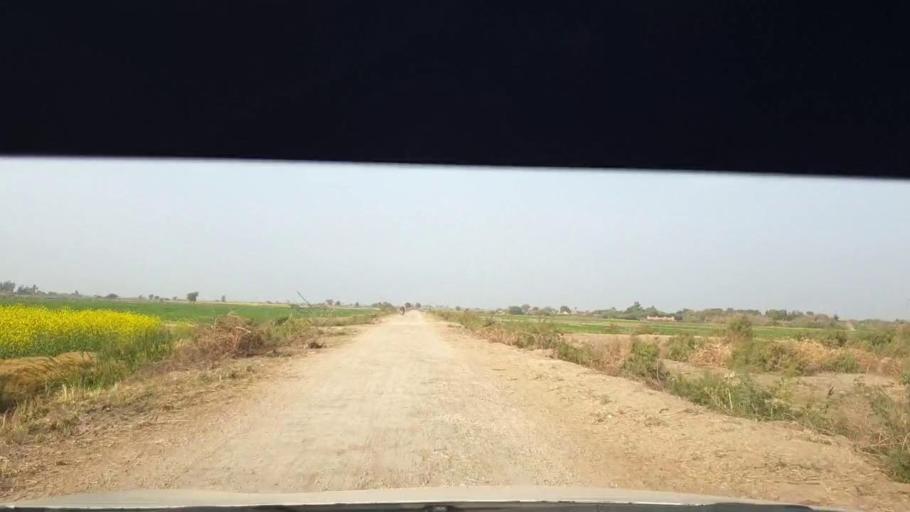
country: PK
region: Sindh
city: Berani
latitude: 25.7548
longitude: 68.9407
